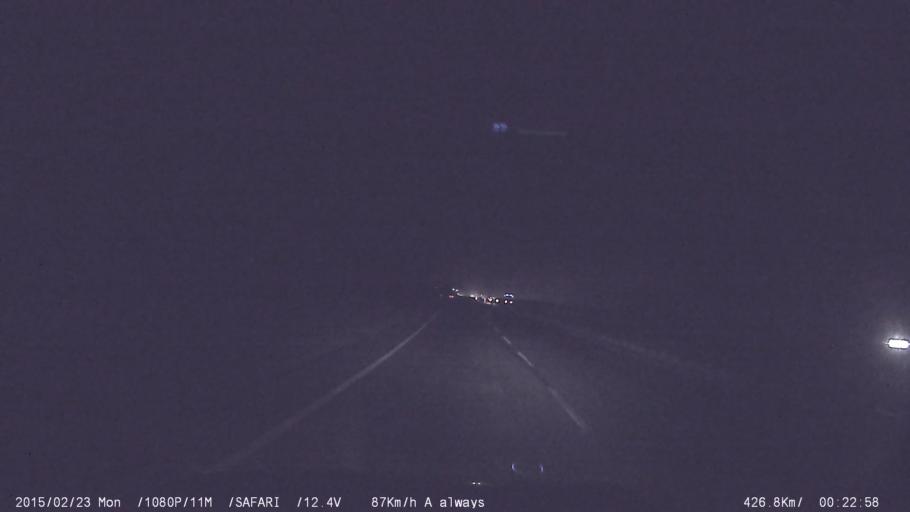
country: IN
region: Tamil Nadu
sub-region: Salem
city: Omalur
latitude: 11.9176
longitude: 78.0610
